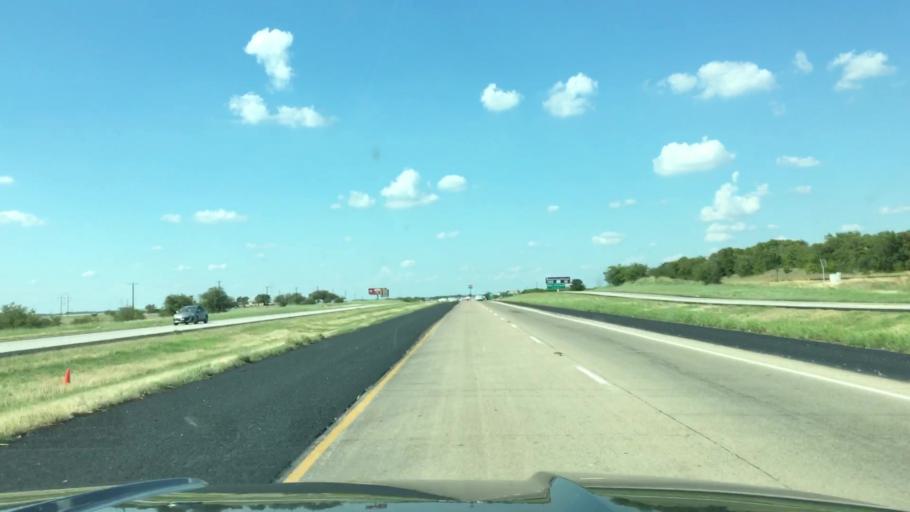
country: US
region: Texas
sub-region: Wise County
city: New Fairview
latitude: 33.0841
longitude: -97.4721
